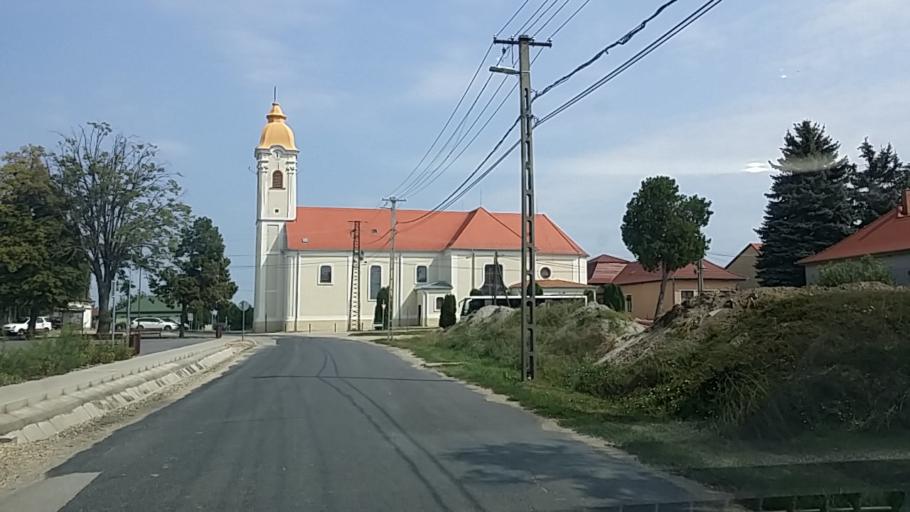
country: HU
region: Gyor-Moson-Sopron
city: Bosarkany
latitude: 47.6903
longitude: 17.2473
